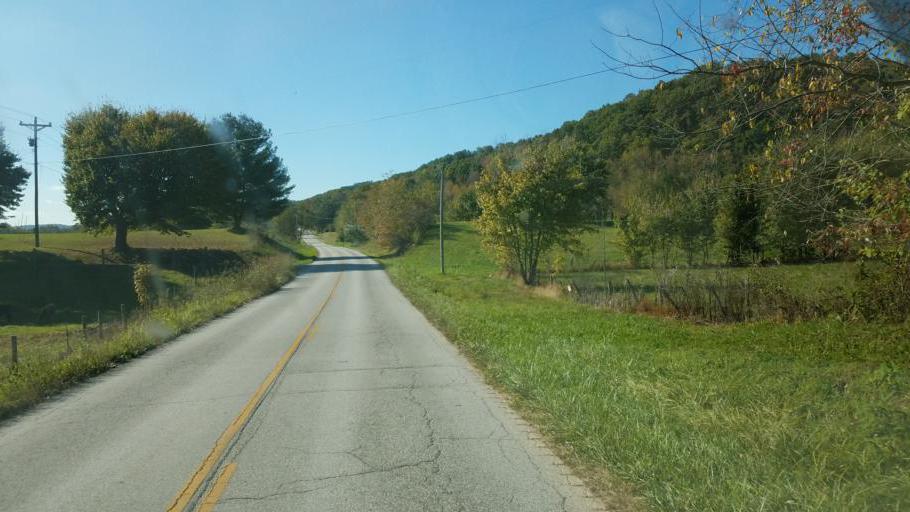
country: US
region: Kentucky
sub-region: Fleming County
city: Flemingsburg
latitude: 38.4684
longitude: -83.5484
